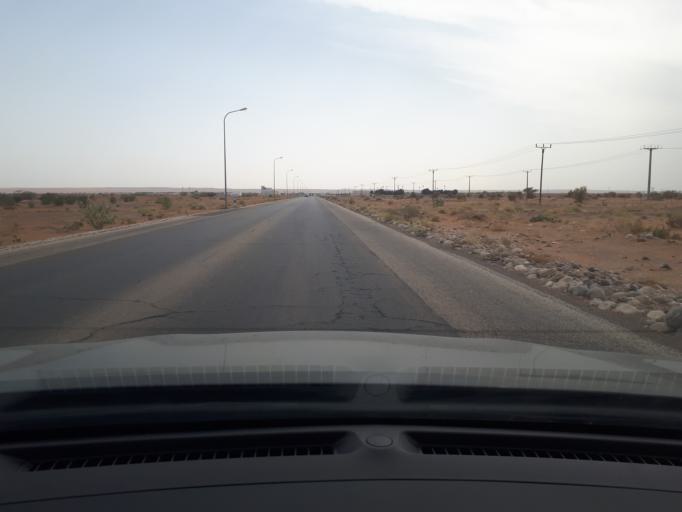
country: OM
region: Ash Sharqiyah
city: Badiyah
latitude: 22.4570
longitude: 58.8424
